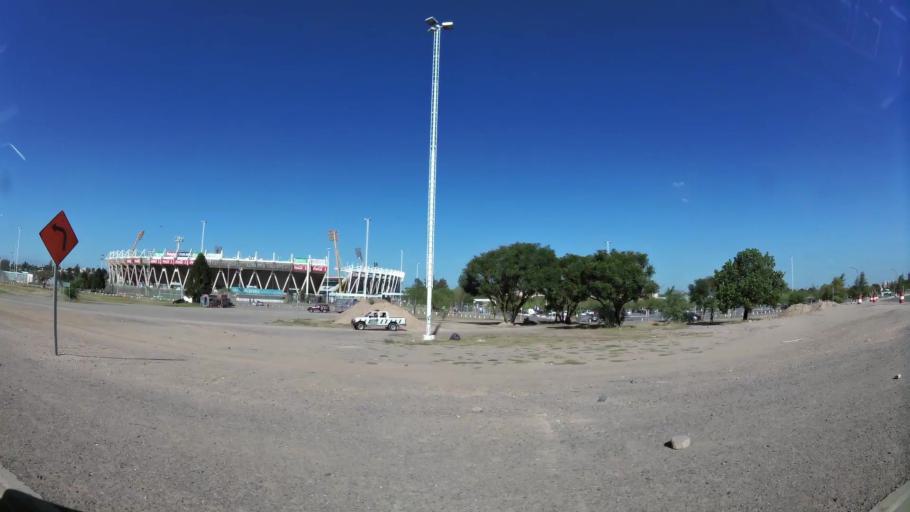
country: AR
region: Cordoba
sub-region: Departamento de Capital
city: Cordoba
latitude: -31.3691
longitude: -64.2501
